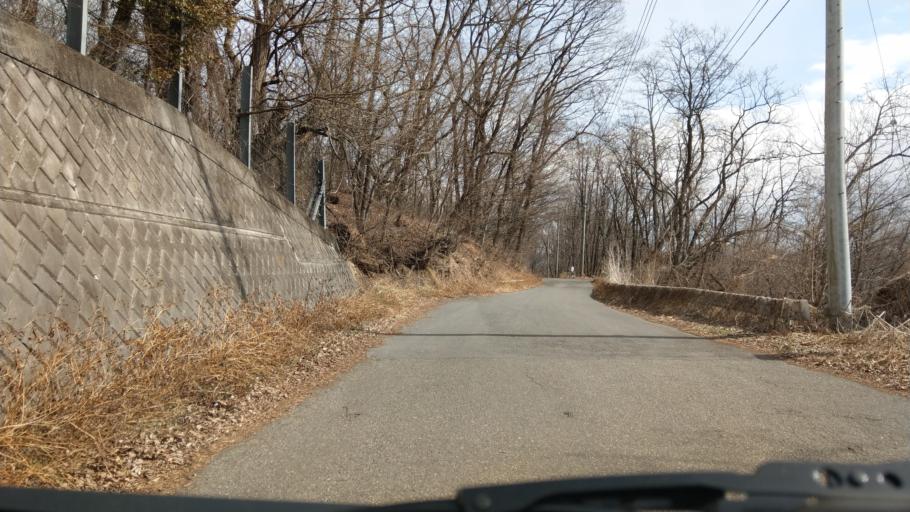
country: JP
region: Nagano
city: Komoro
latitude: 36.2862
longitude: 138.4086
